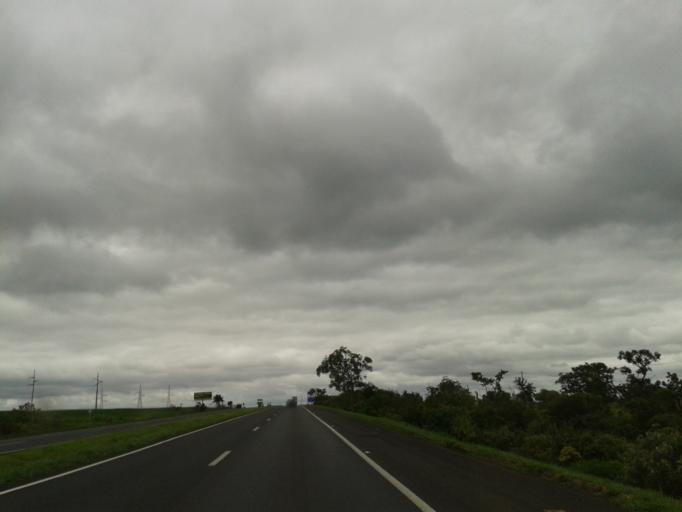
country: BR
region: Minas Gerais
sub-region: Uberlandia
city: Uberlandia
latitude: -19.0272
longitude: -48.2032
